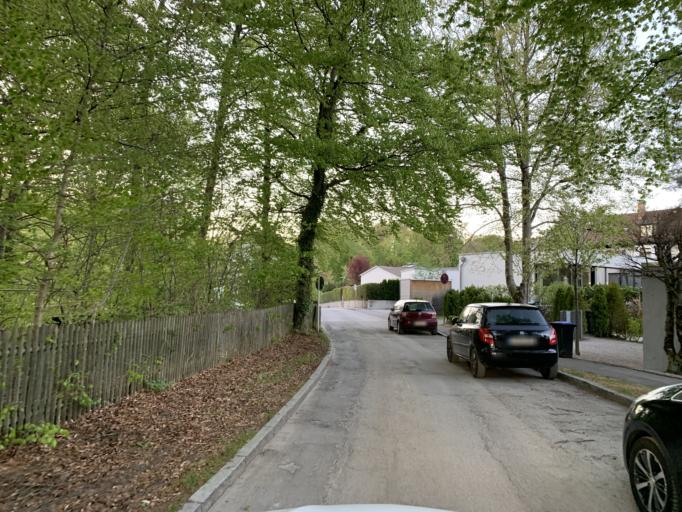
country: DE
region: Bavaria
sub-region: Upper Bavaria
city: Starnberg
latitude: 48.0005
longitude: 11.3337
